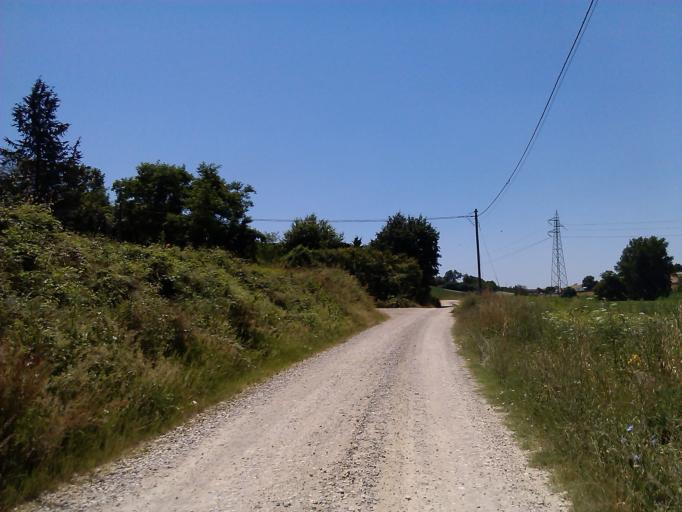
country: IT
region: Umbria
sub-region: Provincia di Terni
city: Ficulle
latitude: 42.8451
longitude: 12.0422
